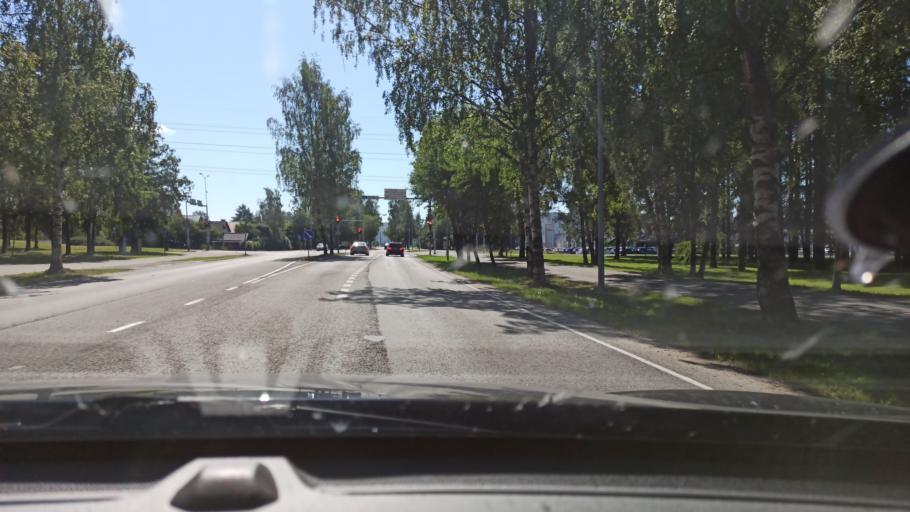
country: FI
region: Northern Ostrobothnia
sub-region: Oulu
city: Oulu
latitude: 65.0391
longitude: 25.4421
